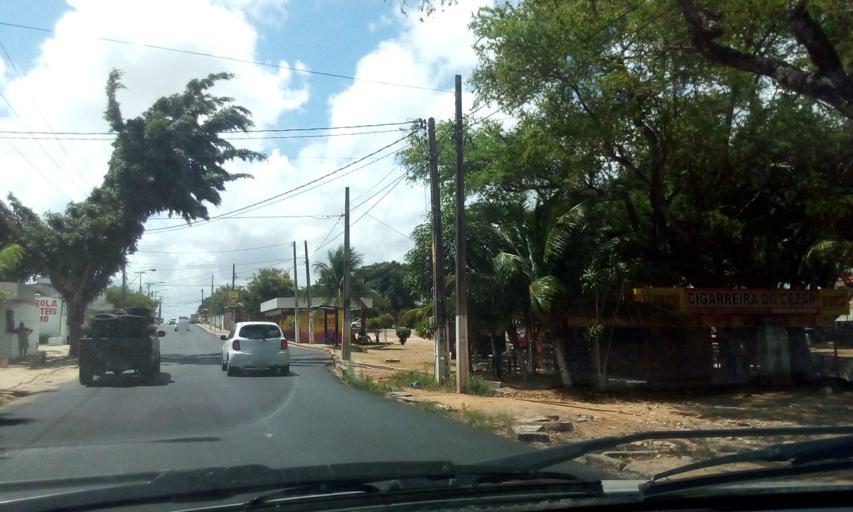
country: BR
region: Rio Grande do Norte
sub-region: Natal
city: Natal
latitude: -5.8572
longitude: -35.2058
